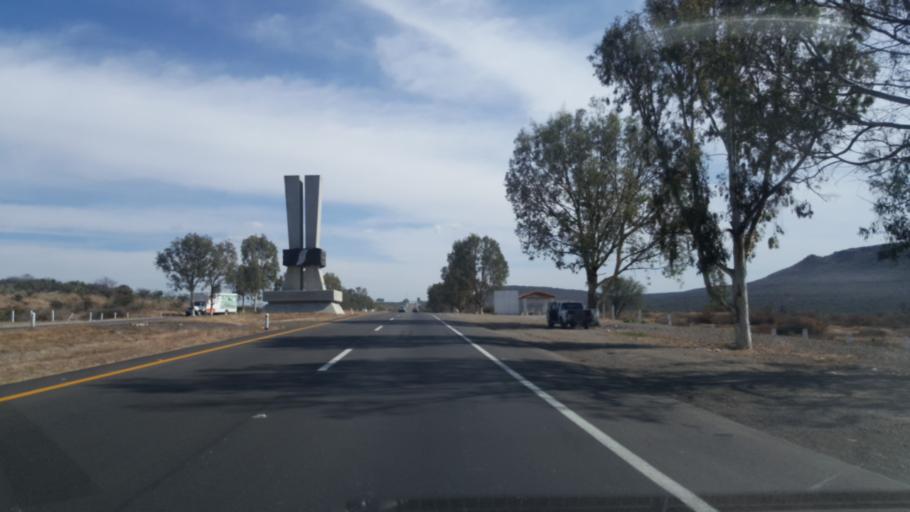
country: MX
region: Jalisco
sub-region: Lagos de Moreno
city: Cristeros [Fraccionamiento]
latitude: 21.2761
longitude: -101.9842
